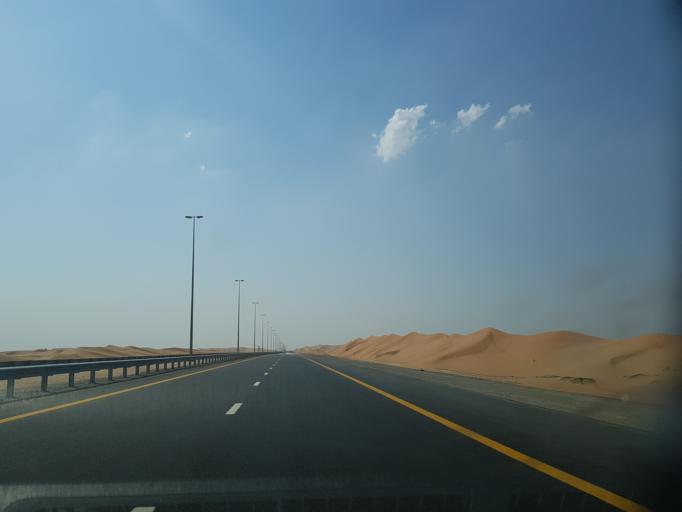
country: AE
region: Ash Shariqah
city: Adh Dhayd
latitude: 25.2569
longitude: 55.7204
